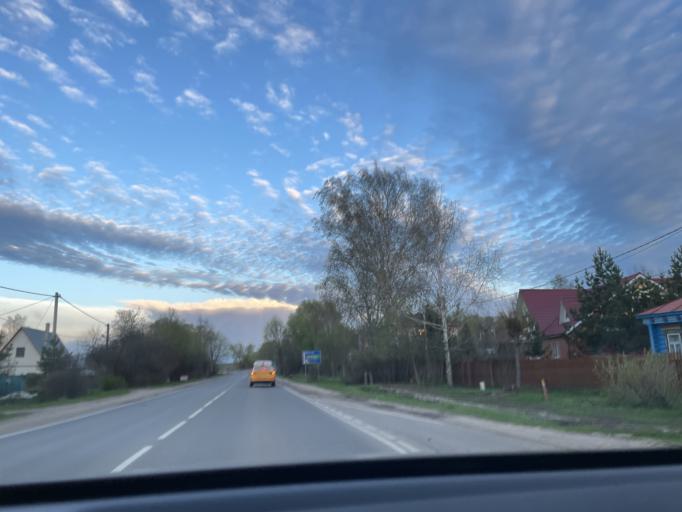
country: RU
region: Moskovskaya
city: Serpukhov
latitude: 54.8615
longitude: 37.4735
